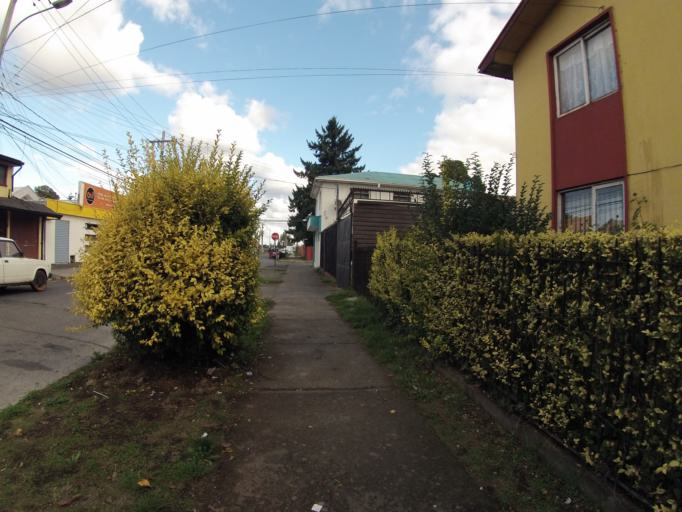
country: CL
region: Araucania
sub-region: Provincia de Cautin
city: Temuco
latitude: -38.7427
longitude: -72.5956
